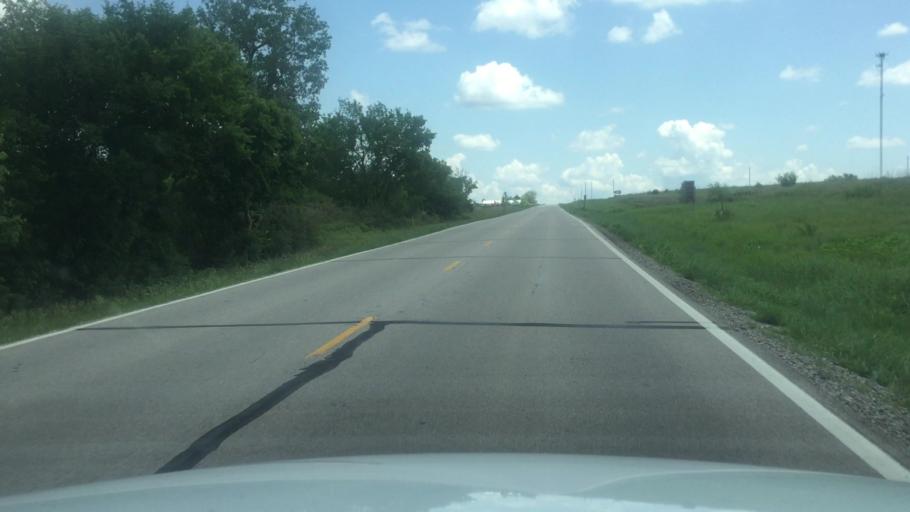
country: US
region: Kansas
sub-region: Brown County
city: Horton
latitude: 39.6674
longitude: -95.6246
